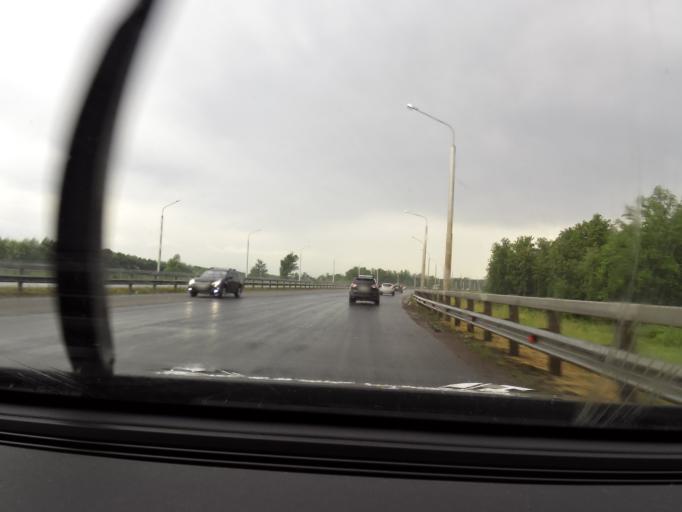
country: RU
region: Bashkortostan
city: Mikhaylovka
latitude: 54.7827
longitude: 55.9125
